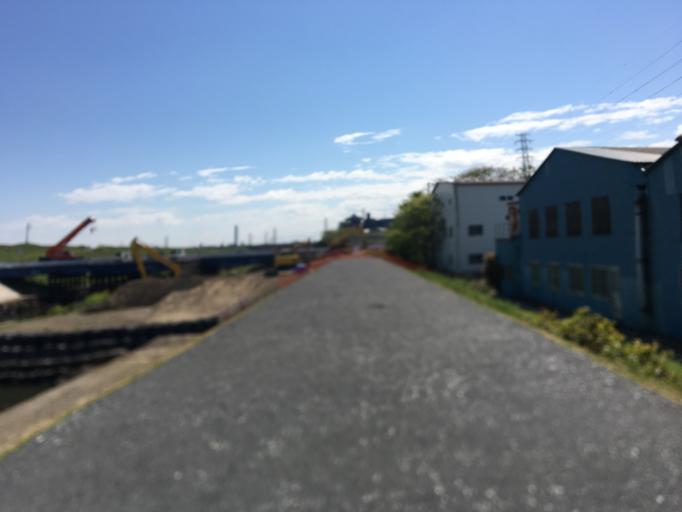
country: JP
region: Saitama
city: Wako
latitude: 35.7989
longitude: 139.6383
